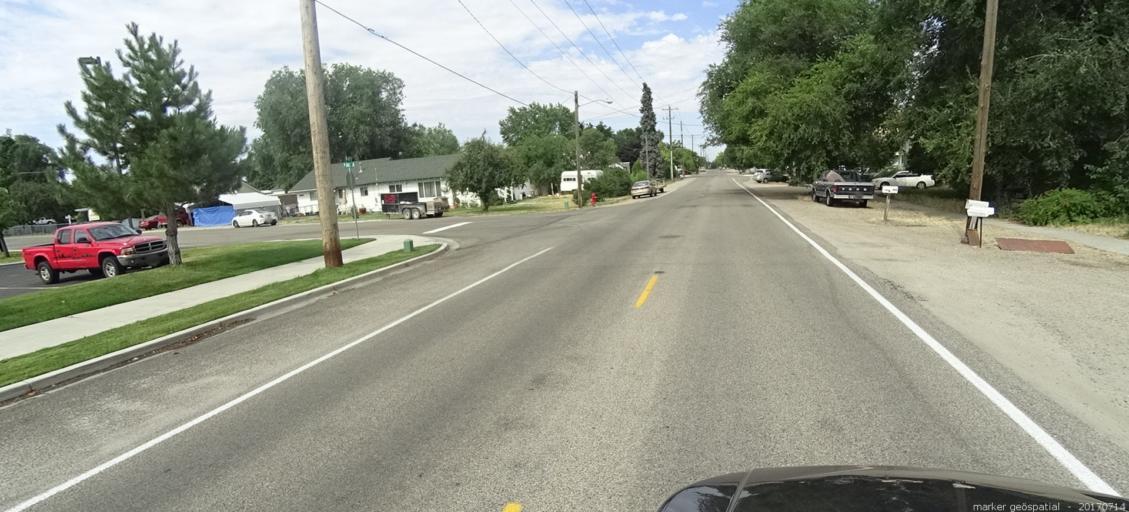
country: US
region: Idaho
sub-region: Ada County
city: Kuna
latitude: 43.4917
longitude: -116.4148
